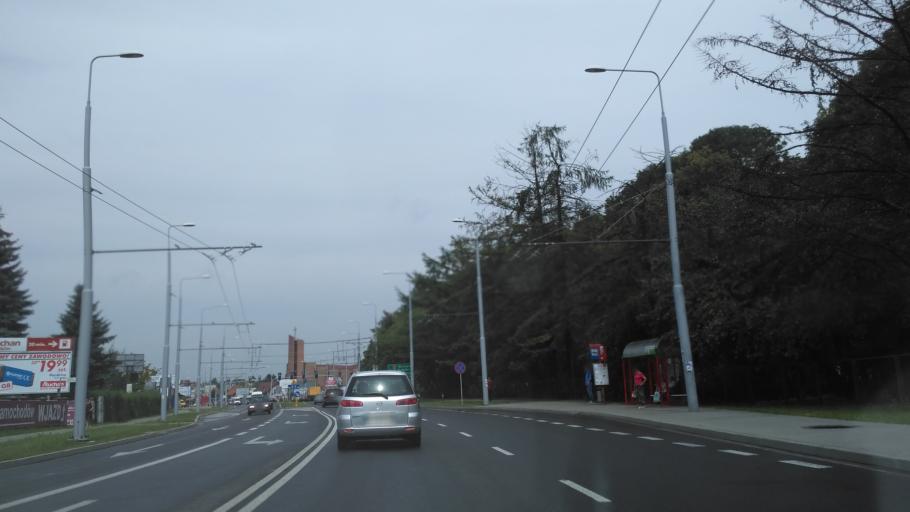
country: PL
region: Lublin Voivodeship
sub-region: Powiat lubelski
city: Lublin
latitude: 51.2054
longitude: 22.5866
